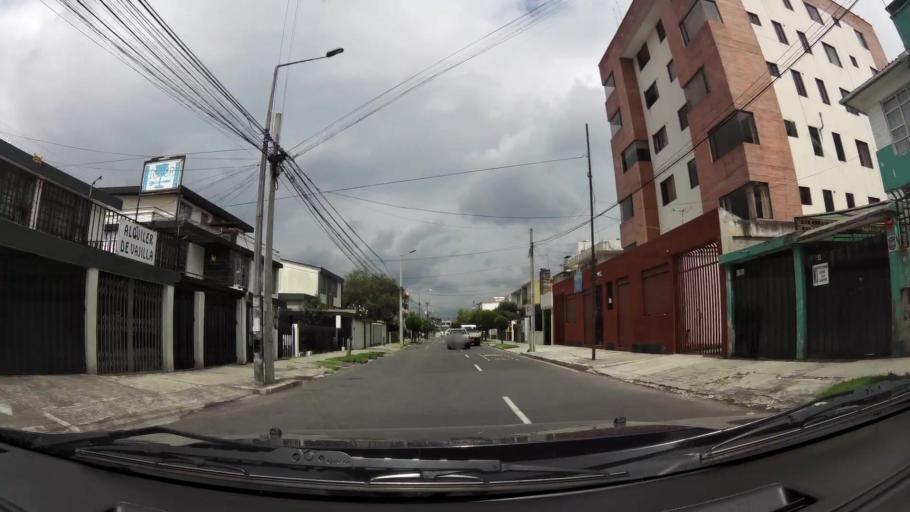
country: EC
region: Pichincha
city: Quito
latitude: -0.1890
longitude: -78.4938
